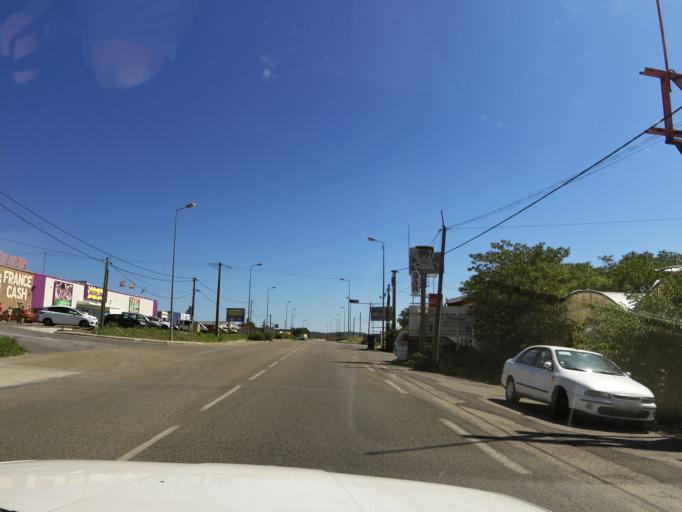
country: FR
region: Languedoc-Roussillon
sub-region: Departement du Gard
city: Saint-Hilaire-de-Brethmas
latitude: 44.0952
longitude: 4.1070
